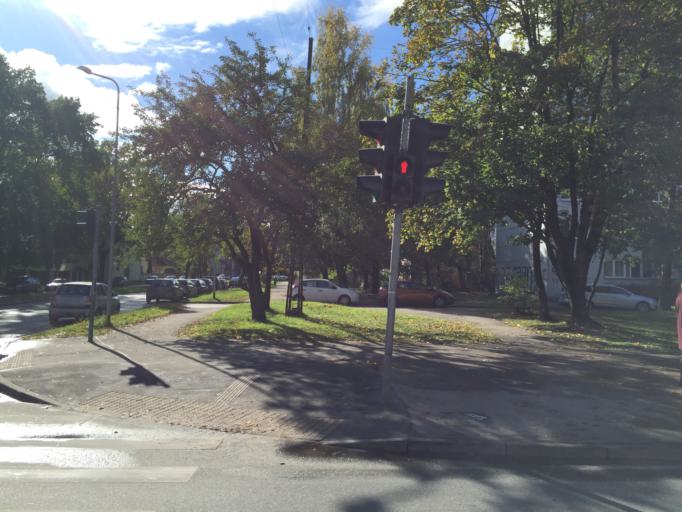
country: LV
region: Marupe
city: Marupe
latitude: 56.9475
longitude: 24.0601
